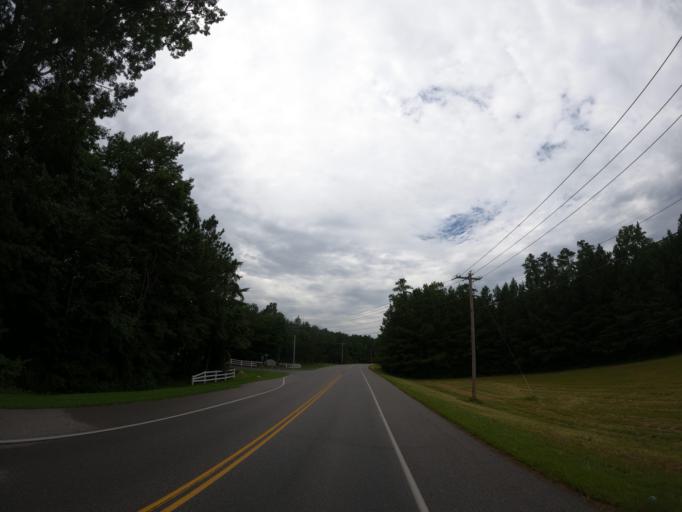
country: US
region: Maryland
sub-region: Saint Mary's County
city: California
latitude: 38.2786
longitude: -76.5491
